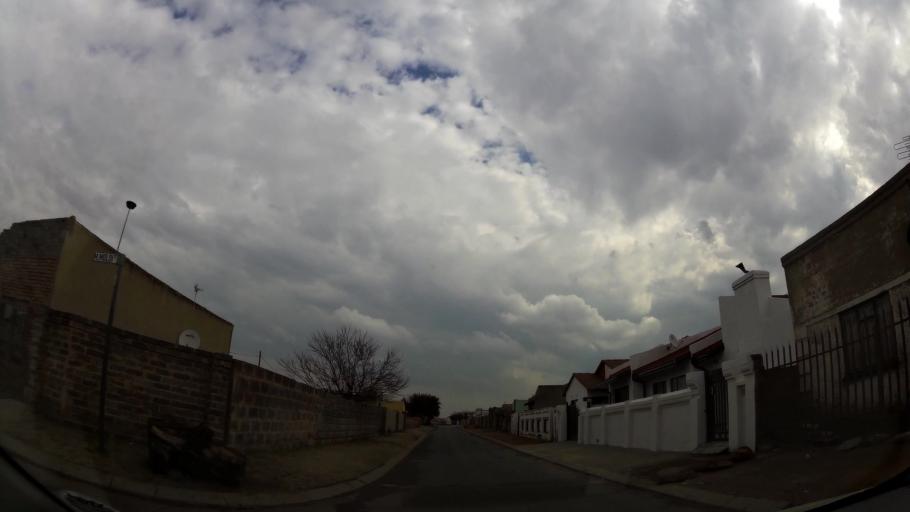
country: ZA
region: Gauteng
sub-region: Ekurhuleni Metropolitan Municipality
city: Germiston
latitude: -26.3841
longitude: 28.1611
